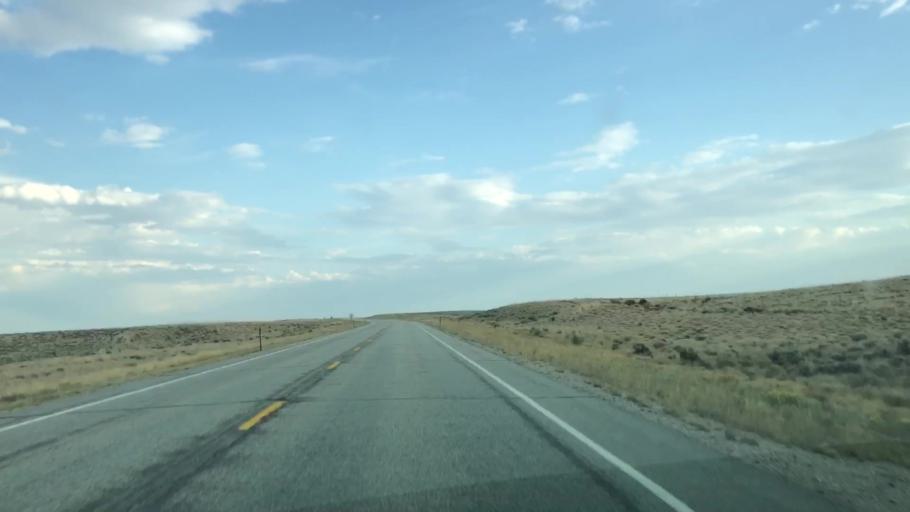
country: US
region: Wyoming
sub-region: Sweetwater County
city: North Rock Springs
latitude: 42.2830
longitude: -109.4868
